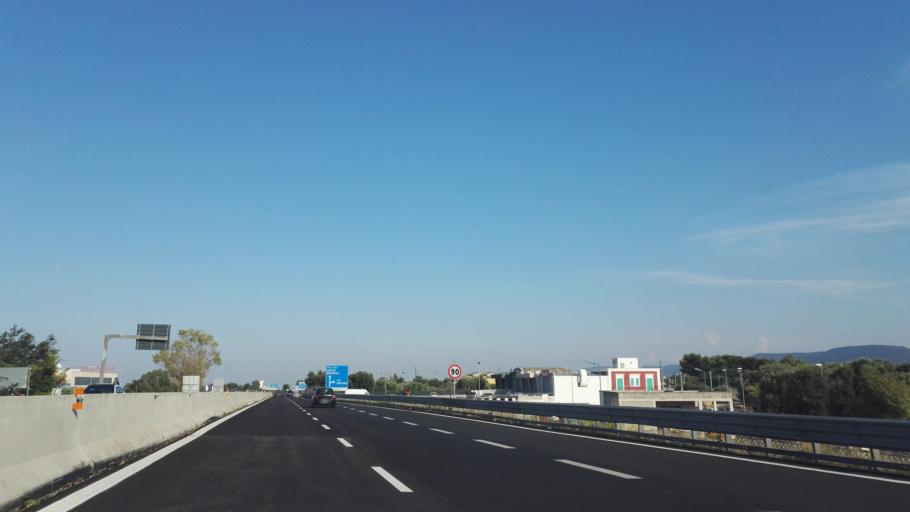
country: IT
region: Apulia
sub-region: Provincia di Brindisi
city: Fasano
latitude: 40.8394
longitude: 17.3755
